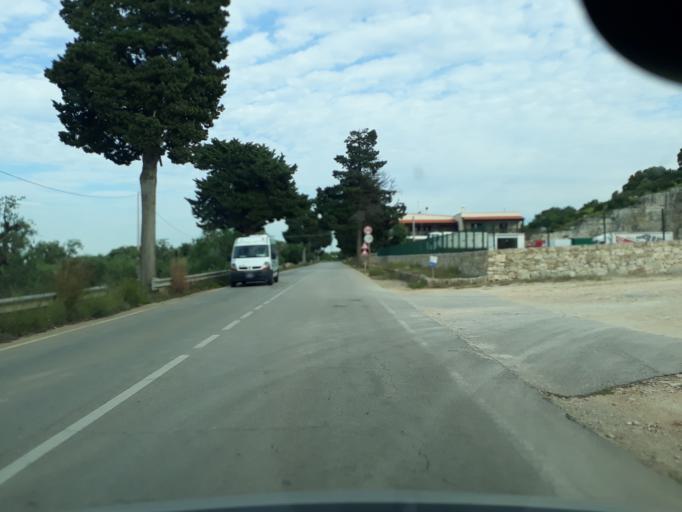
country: IT
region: Apulia
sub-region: Provincia di Brindisi
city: Ostuni
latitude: 40.7486
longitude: 17.5552
